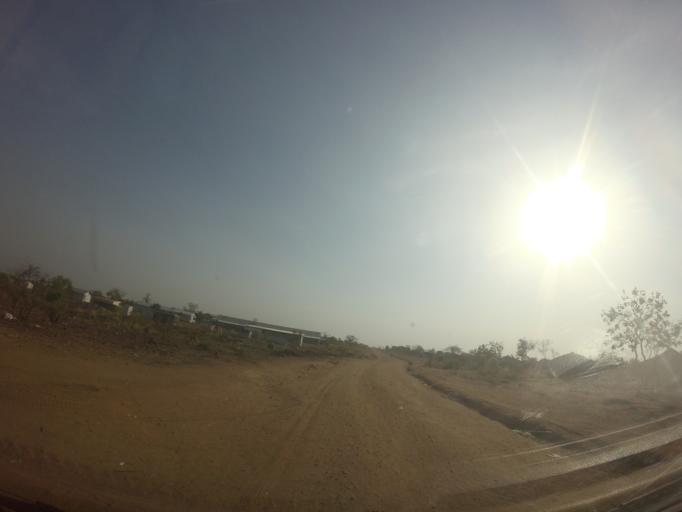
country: UG
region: Northern Region
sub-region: Maracha District
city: Maracha
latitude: 3.1221
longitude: 31.1594
